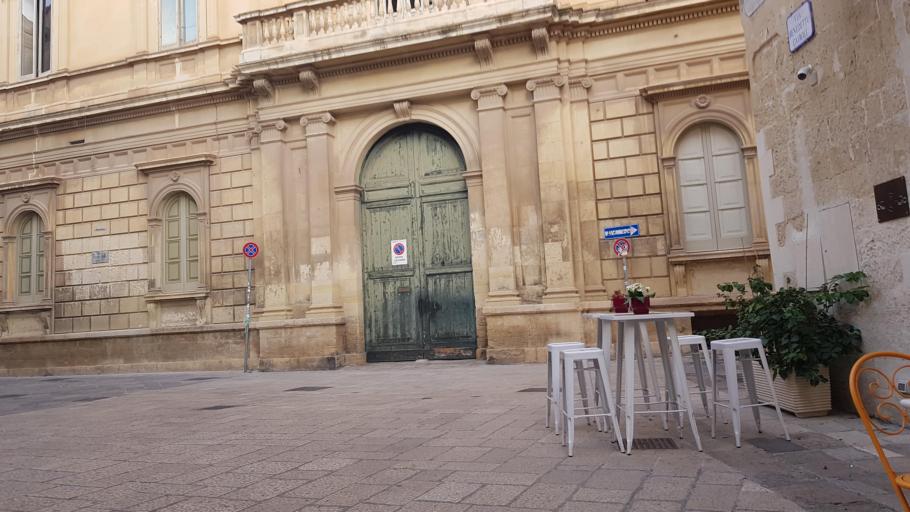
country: IT
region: Apulia
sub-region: Provincia di Lecce
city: Lecce
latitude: 40.3498
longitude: 18.1697
